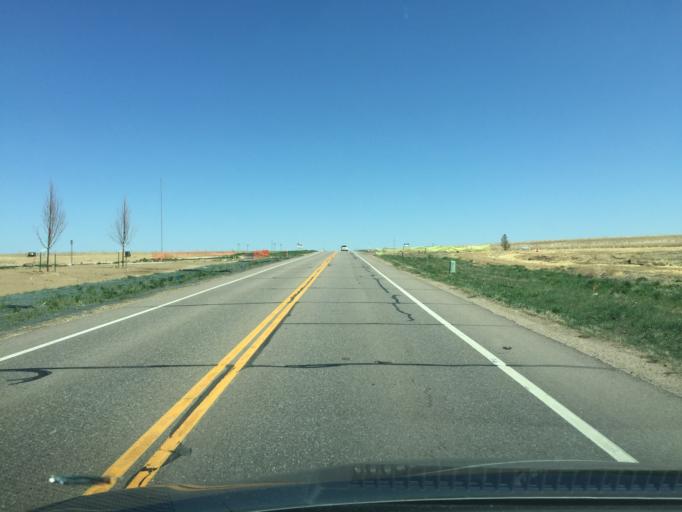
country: US
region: Colorado
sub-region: Boulder County
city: Erie
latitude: 40.0438
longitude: -105.0286
